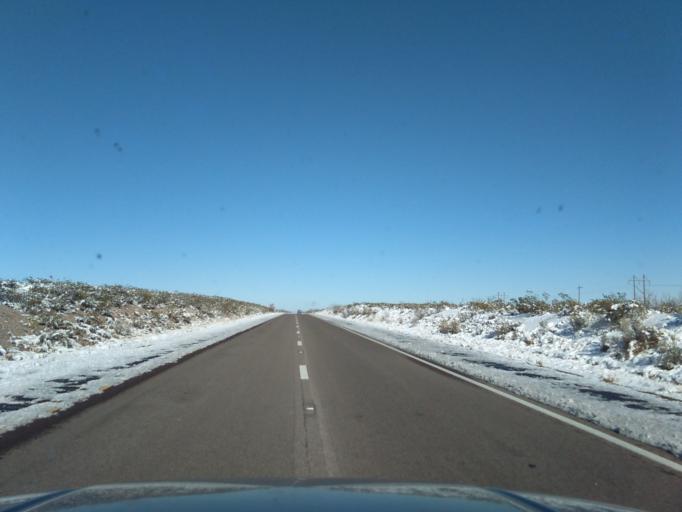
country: US
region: New Mexico
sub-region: Socorro County
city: Socorro
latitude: 33.6657
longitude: -107.0860
